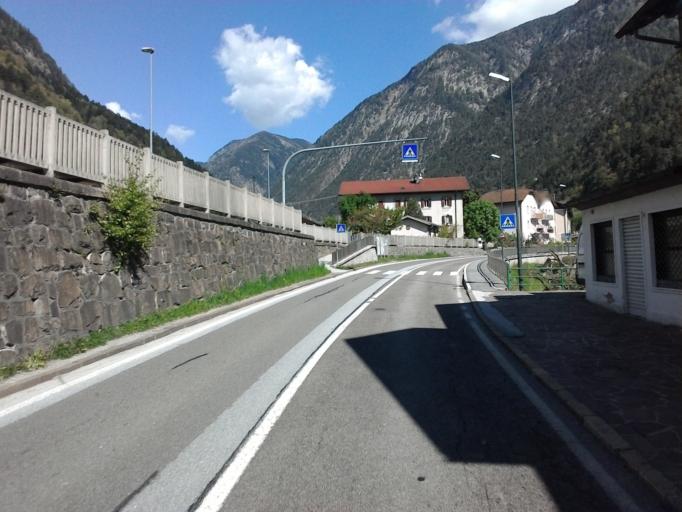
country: IT
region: Trentino-Alto Adige
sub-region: Bolzano
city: Fortezza
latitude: 46.7870
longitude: 11.6119
